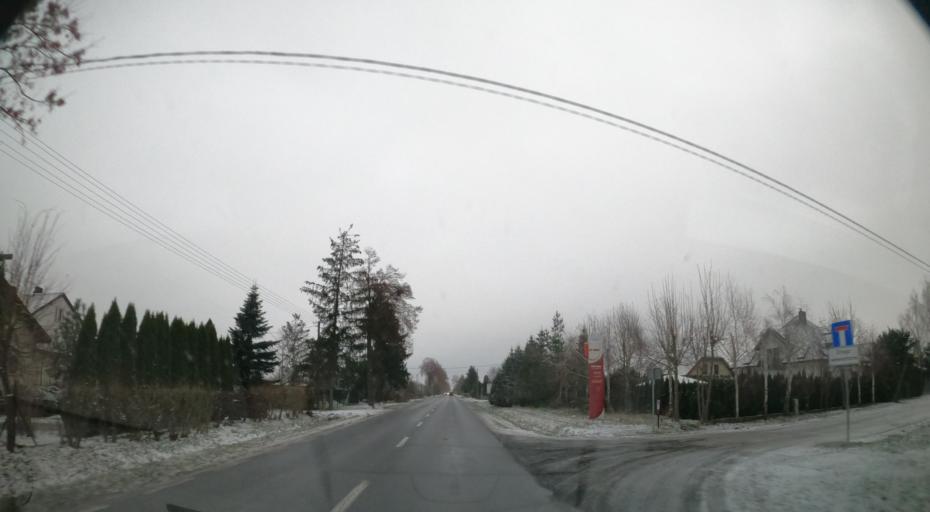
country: PL
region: Masovian Voivodeship
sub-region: Powiat plocki
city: Maszewo Duze
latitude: 52.5633
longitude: 19.6342
